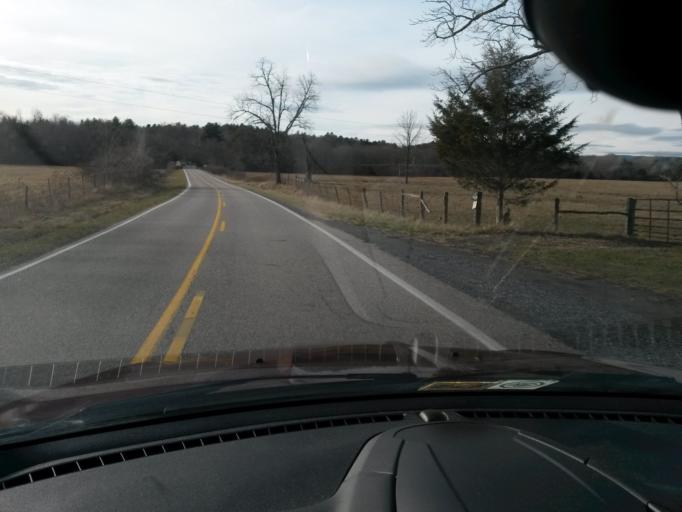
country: US
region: Virginia
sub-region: Bath County
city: Warm Springs
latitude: 38.0022
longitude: -79.5752
